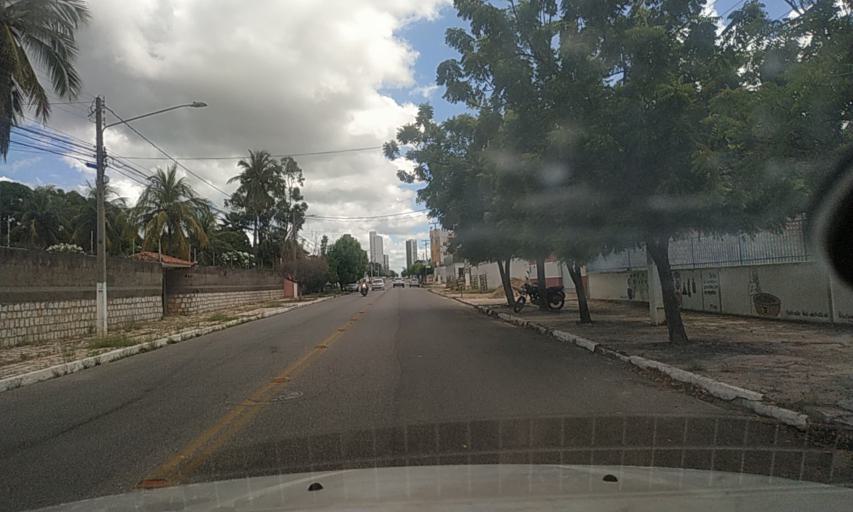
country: BR
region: Rio Grande do Norte
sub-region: Mossoro
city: Mossoro
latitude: -5.1847
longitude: -37.3526
